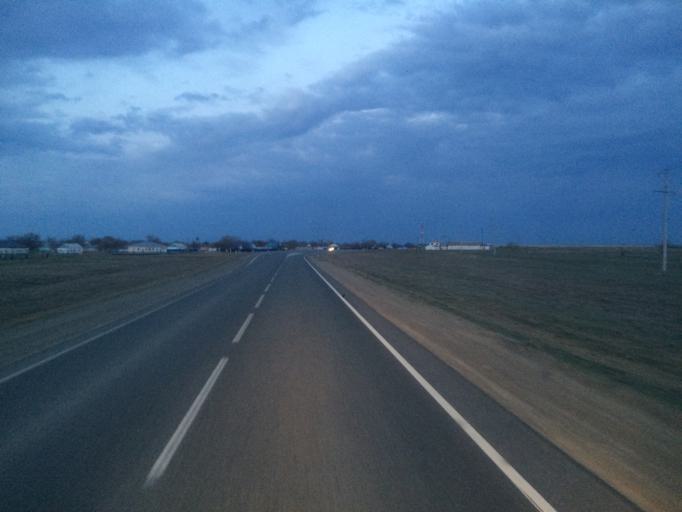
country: KZ
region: Aqtoebe
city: Martuk
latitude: 50.6401
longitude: 56.6857
